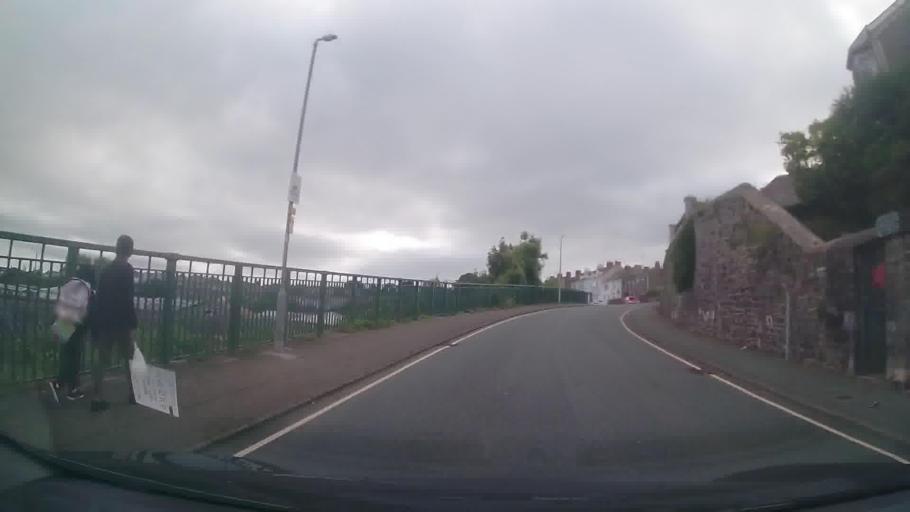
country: GB
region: Wales
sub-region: Pembrokeshire
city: Milford Haven
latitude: 51.7140
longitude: -5.0428
